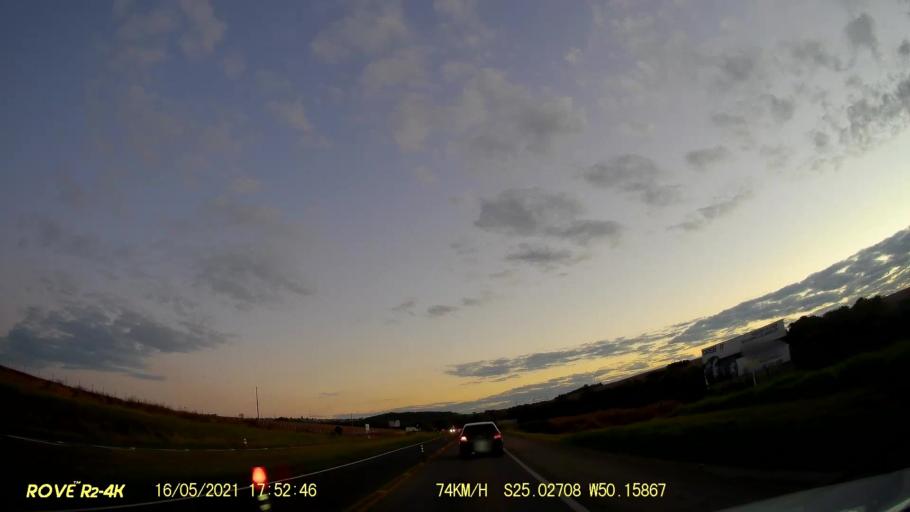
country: BR
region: Parana
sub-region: Ponta Grossa
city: Ponta Grossa
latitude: -25.0272
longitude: -50.1584
